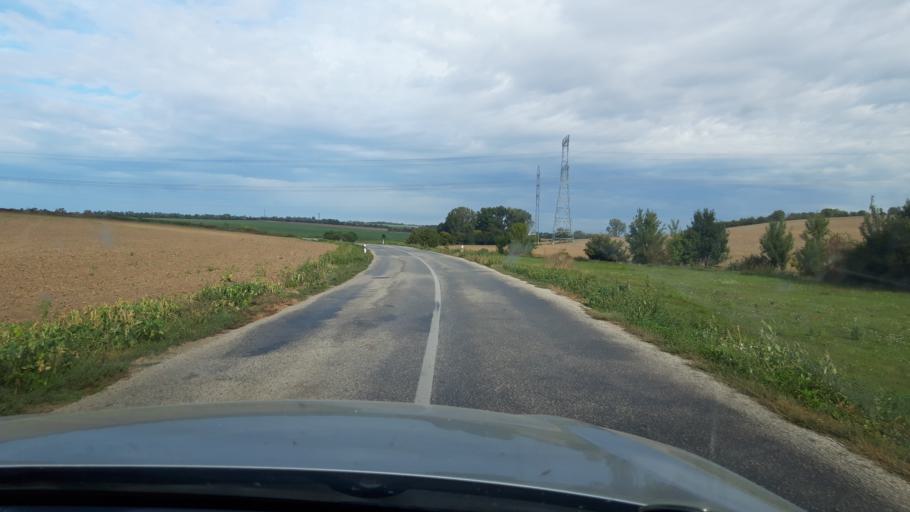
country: SK
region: Nitriansky
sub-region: Okres Nitra
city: Vrable
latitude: 48.1160
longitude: 18.3359
